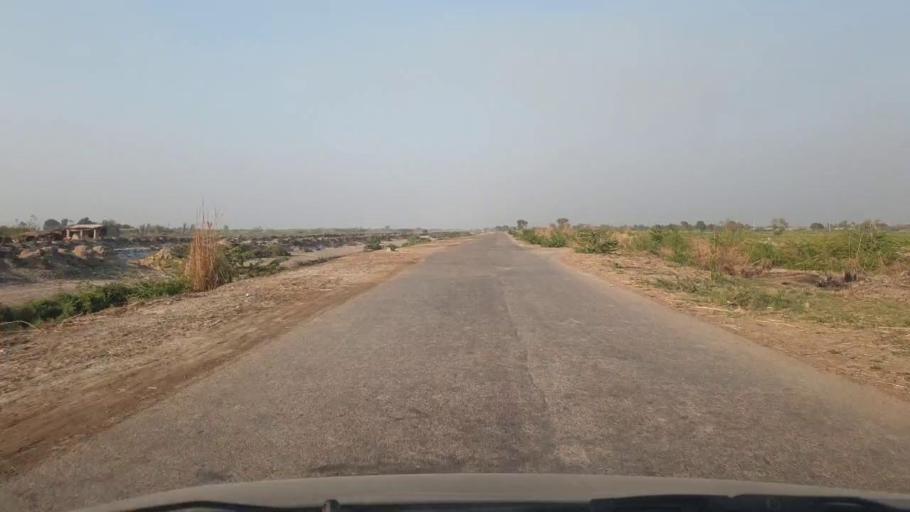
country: PK
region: Sindh
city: Mirwah Gorchani
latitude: 25.3495
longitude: 69.1722
